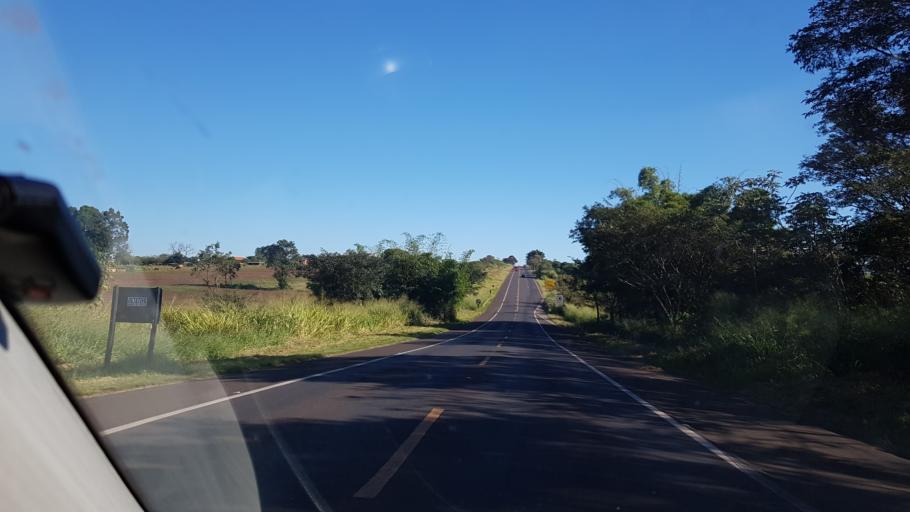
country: BR
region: Sao Paulo
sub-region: Assis
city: Assis
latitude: -22.6036
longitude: -50.4761
